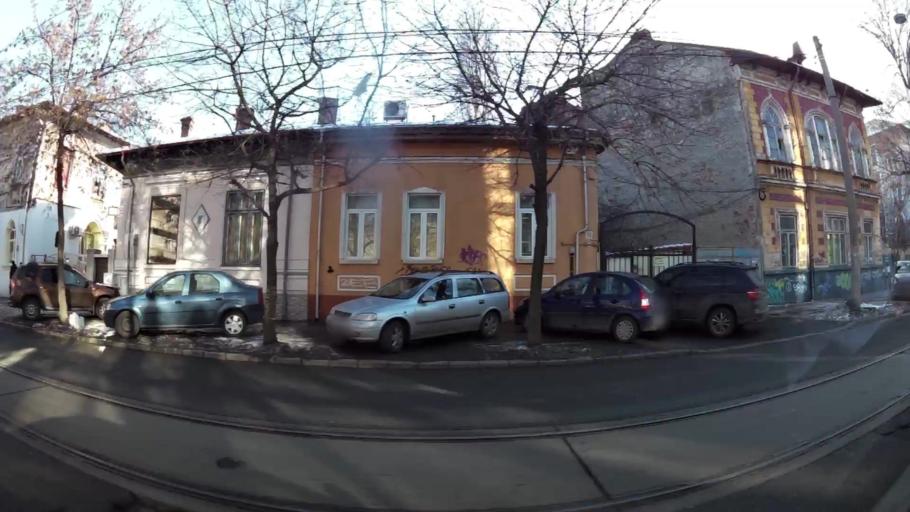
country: RO
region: Bucuresti
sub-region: Municipiul Bucuresti
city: Bucharest
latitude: 44.4401
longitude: 26.1270
